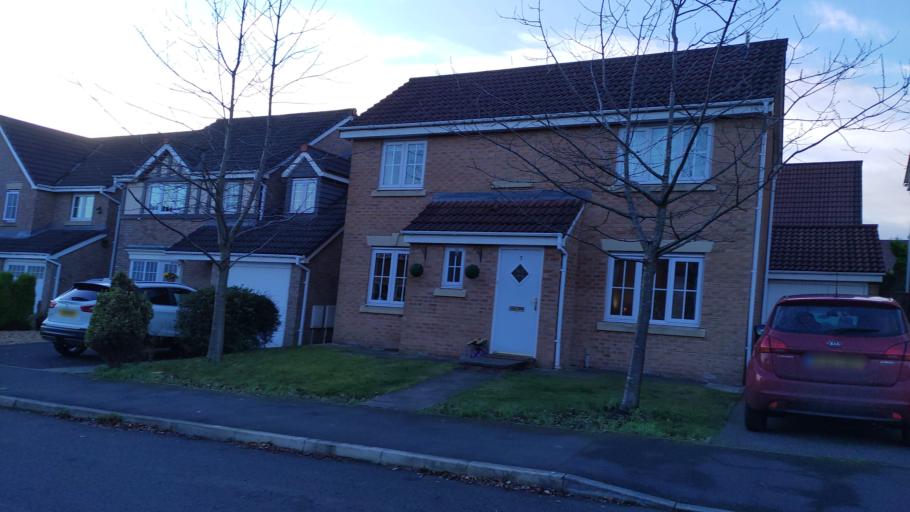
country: GB
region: England
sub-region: Lancashire
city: Clayton-le-Woods
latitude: 53.6850
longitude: -2.6598
